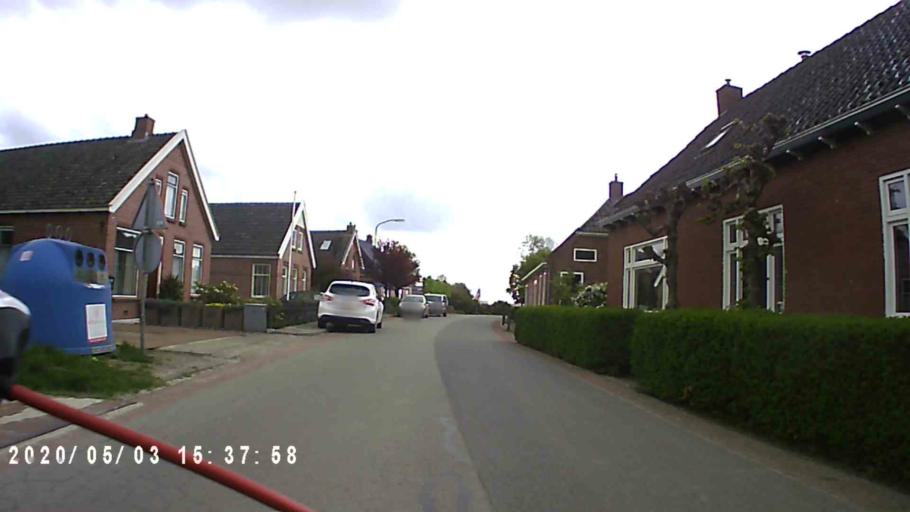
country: NL
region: Groningen
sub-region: Gemeente Zuidhorn
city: Oldehove
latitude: 53.3309
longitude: 6.4494
